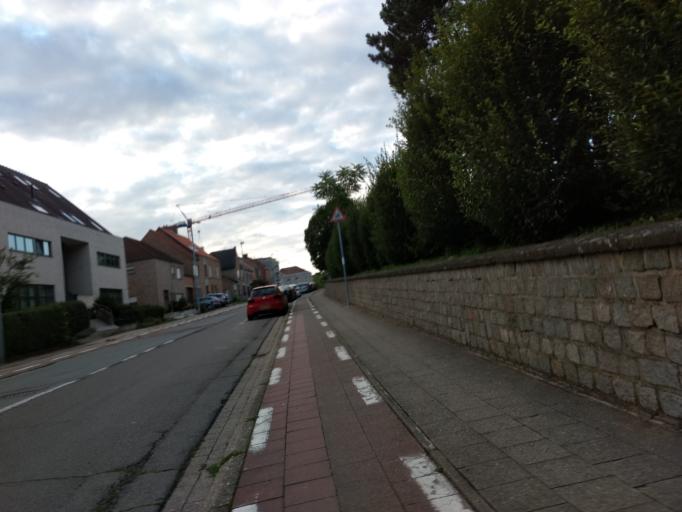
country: BE
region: Flanders
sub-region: Provincie Vlaams-Brabant
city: Leuven
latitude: 50.8726
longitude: 4.6733
